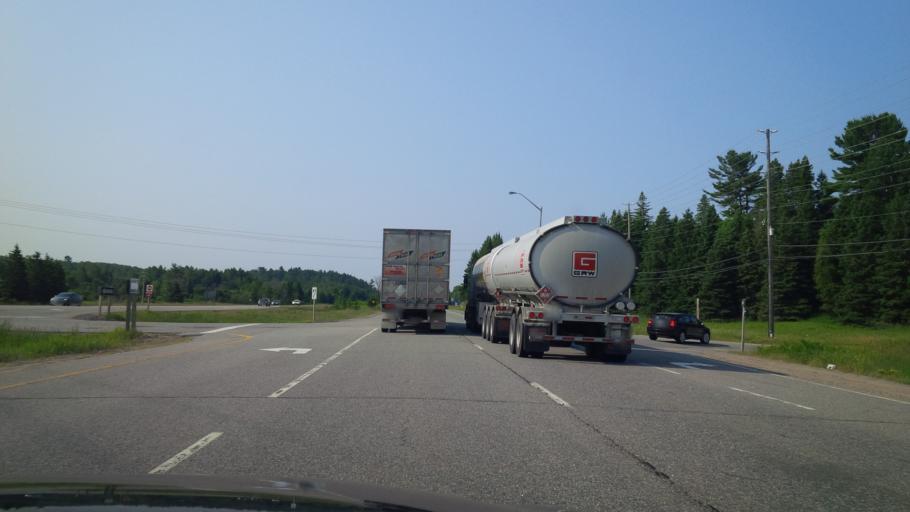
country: CA
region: Ontario
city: Huntsville
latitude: 45.2561
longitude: -79.2966
